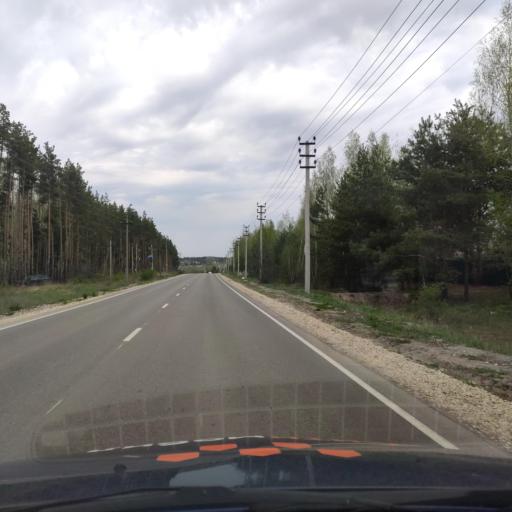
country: RU
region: Voronezj
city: Podgornoye
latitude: 51.8630
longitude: 39.1679
